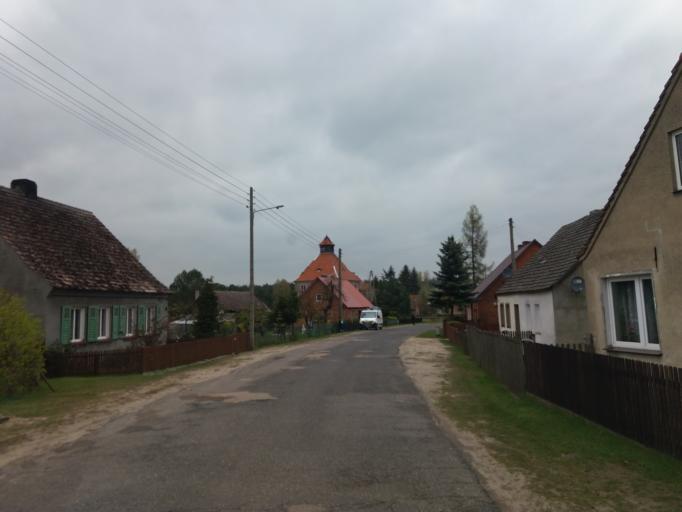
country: PL
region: Lubusz
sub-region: Powiat strzelecko-drezdenecki
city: Dobiegniew
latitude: 53.0855
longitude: 15.7807
